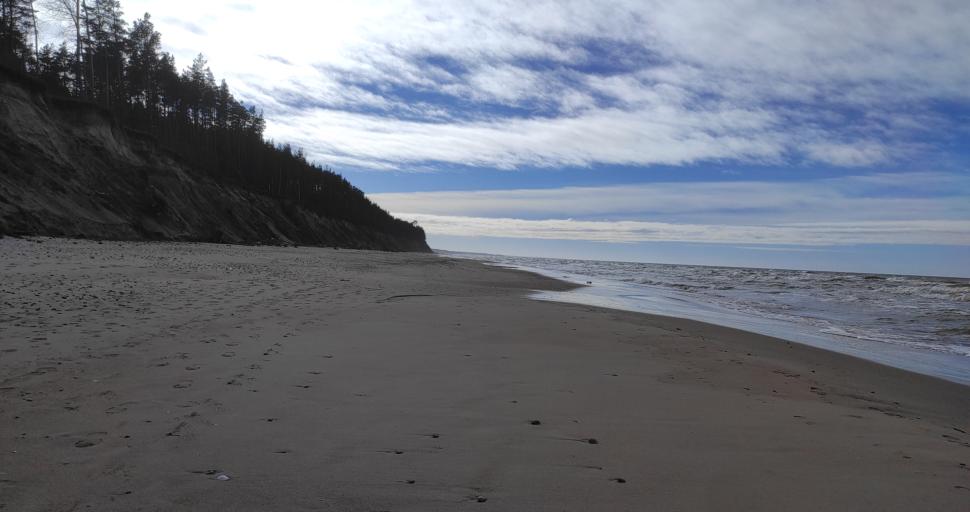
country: LV
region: Alsunga
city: Alsunga
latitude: 57.0261
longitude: 21.3943
